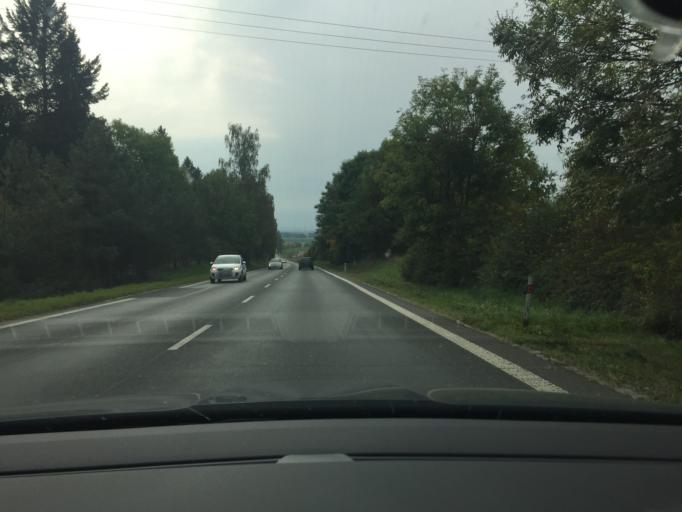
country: CZ
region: Jihocesky
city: Mirovice
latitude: 49.5454
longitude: 14.0816
